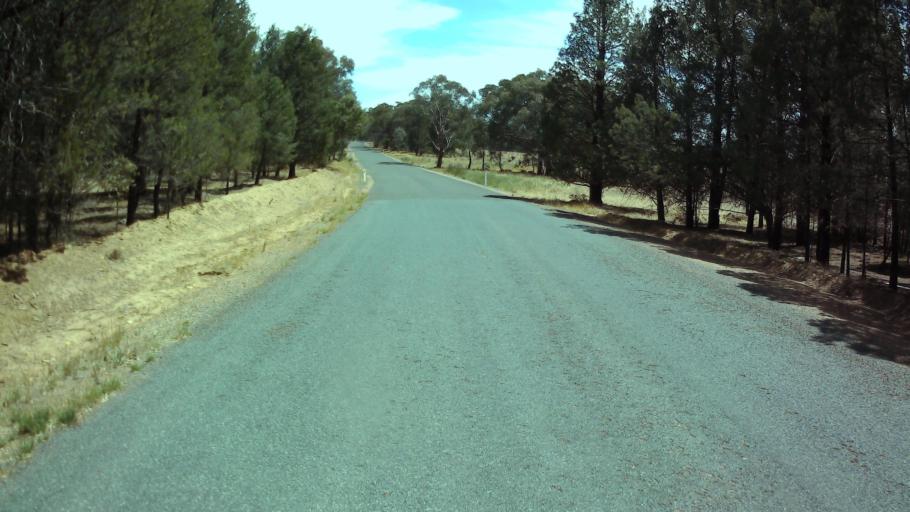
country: AU
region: New South Wales
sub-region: Weddin
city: Grenfell
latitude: -33.7718
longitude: 148.2062
